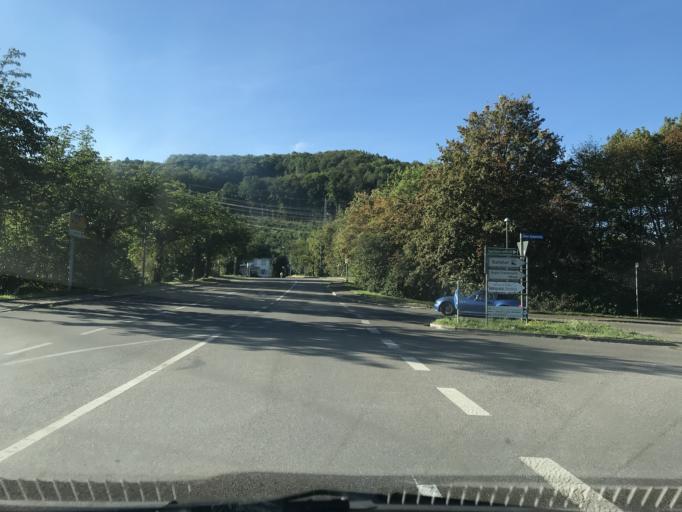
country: DE
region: Baden-Wuerttemberg
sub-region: Freiburg Region
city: Loerrach
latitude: 47.6314
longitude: 7.6829
